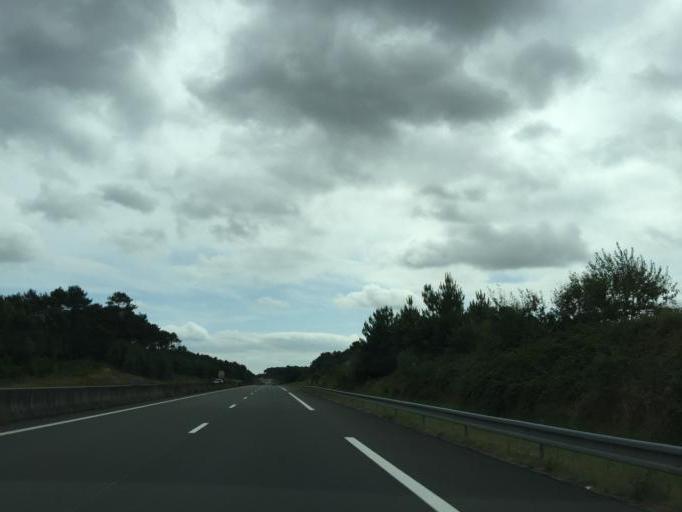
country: FR
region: Pays de la Loire
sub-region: Departement de la Sarthe
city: Mayet
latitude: 47.7640
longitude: 0.3142
